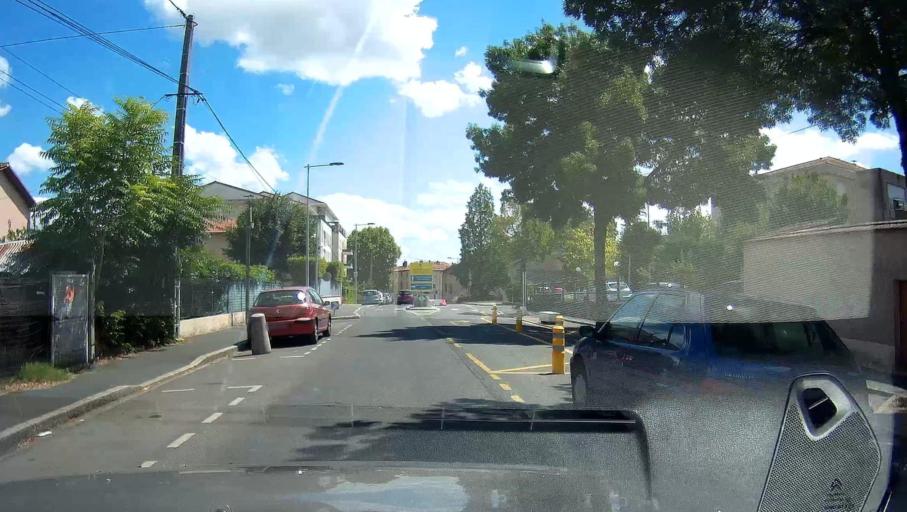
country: FR
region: Rhone-Alpes
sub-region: Departement du Rhone
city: Villefranche-sur-Saone
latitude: 45.9854
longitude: 4.7283
